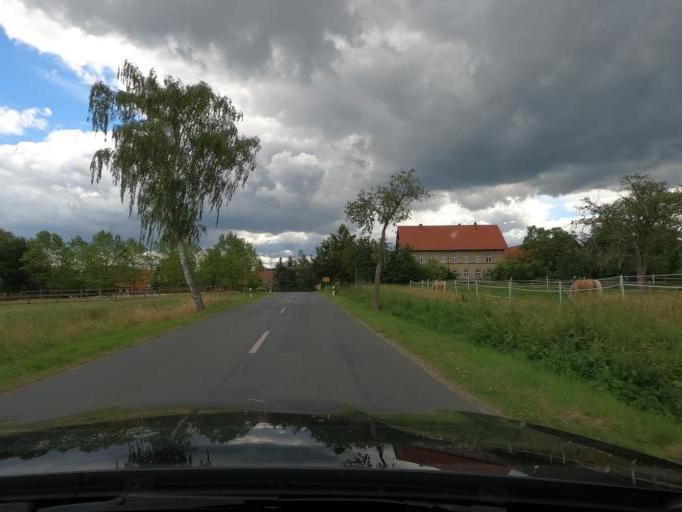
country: DE
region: Lower Saxony
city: Sehlde
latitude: 52.0419
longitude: 10.2643
